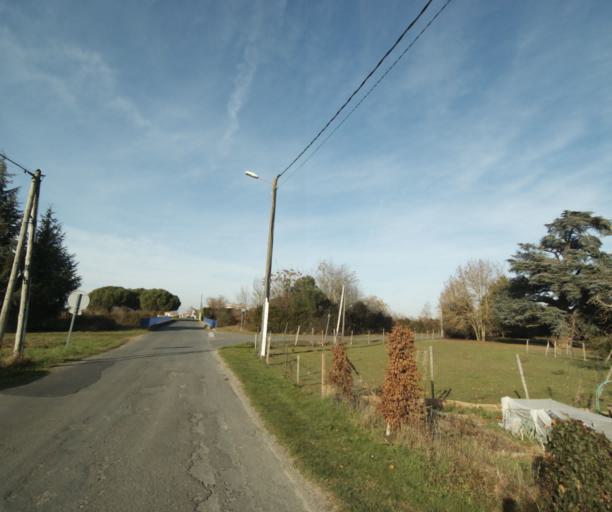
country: FR
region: Poitou-Charentes
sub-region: Departement de la Charente-Maritime
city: Les Gonds
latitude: 45.7380
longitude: -0.6017
